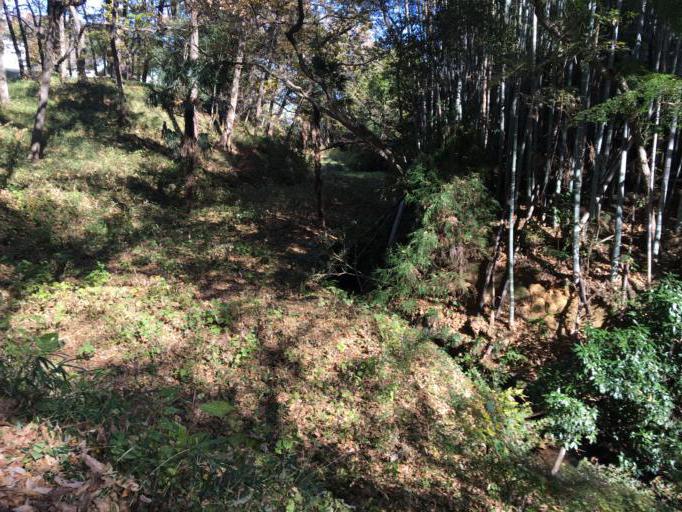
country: JP
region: Saitama
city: Ogawa
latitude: 36.0356
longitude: 139.3238
